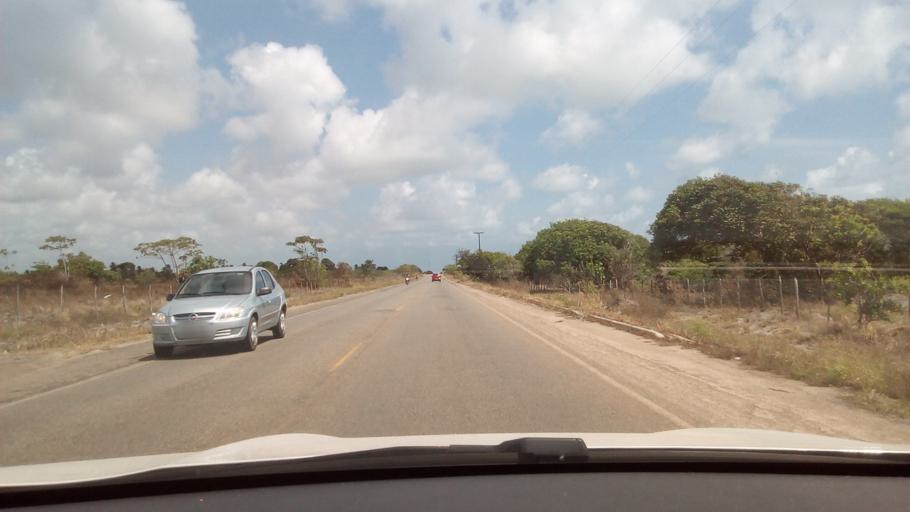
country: BR
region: Paraiba
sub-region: Conde
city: Conde
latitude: -7.2594
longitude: -34.8119
